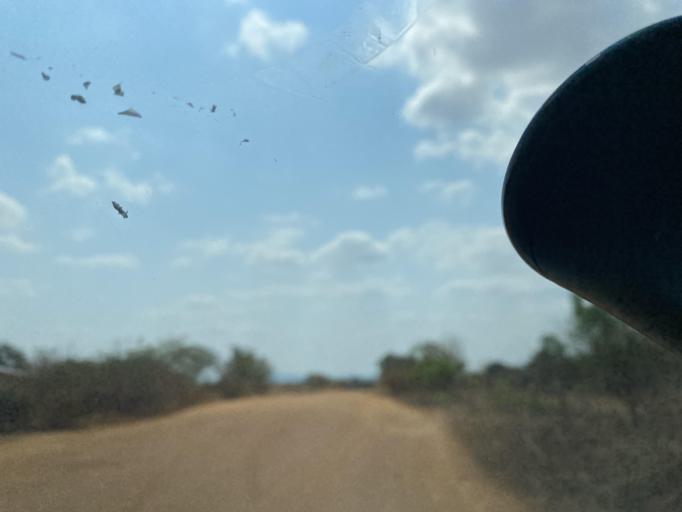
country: ZM
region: Lusaka
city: Chongwe
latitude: -15.5892
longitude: 28.7733
